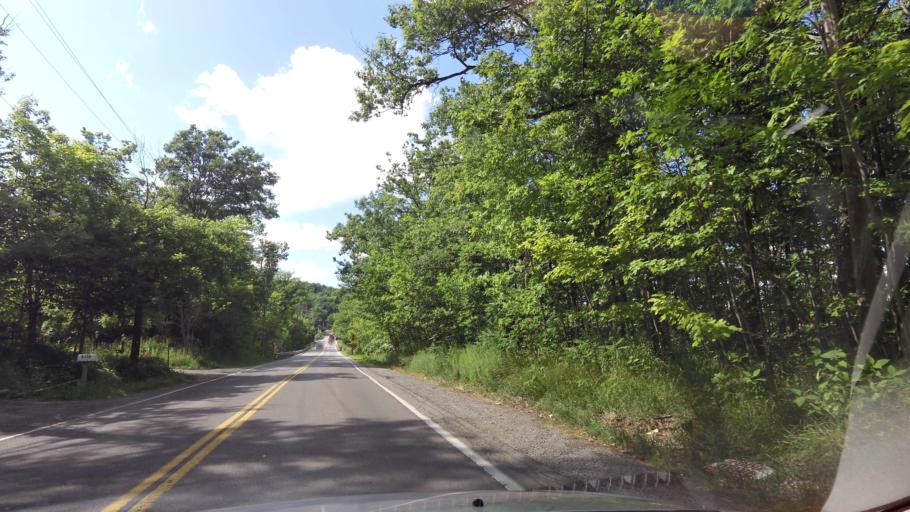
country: CA
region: Ontario
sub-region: Halton
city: Milton
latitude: 43.4656
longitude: -79.9031
